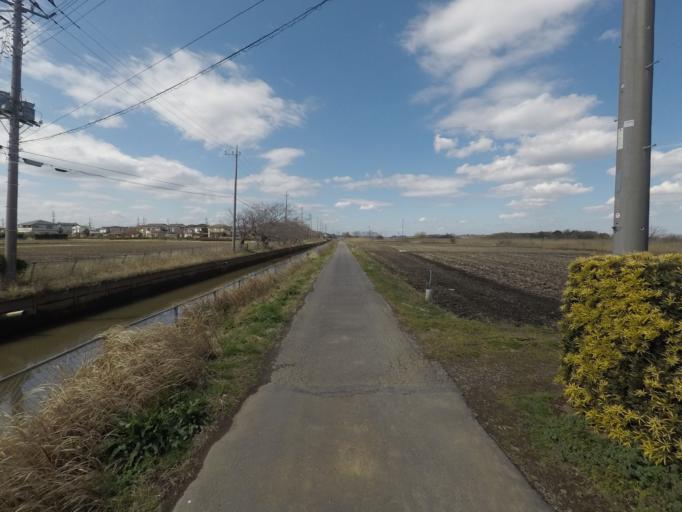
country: JP
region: Ibaraki
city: Fujishiro
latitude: 35.9366
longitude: 140.1274
